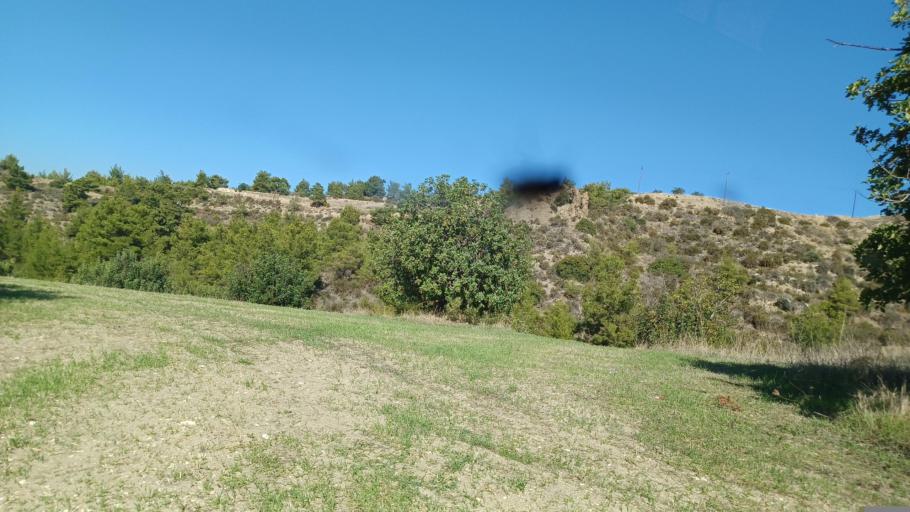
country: CY
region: Pafos
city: Polis
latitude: 35.0333
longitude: 32.4975
